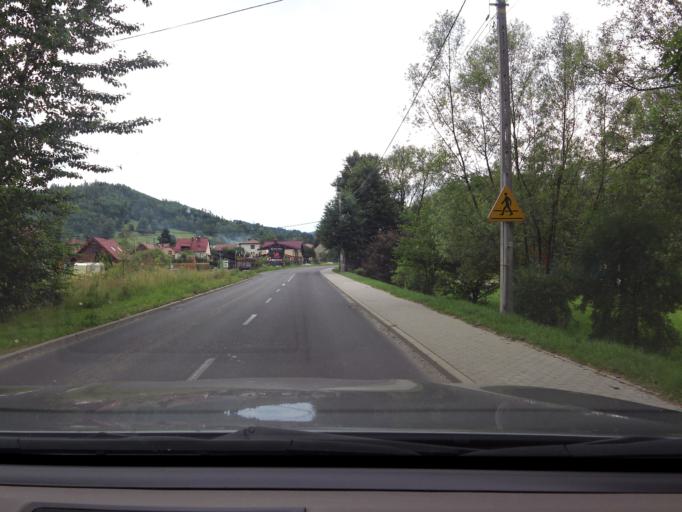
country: PL
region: Silesian Voivodeship
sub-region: Powiat zywiecki
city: Rajcza
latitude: 49.5099
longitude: 19.1133
